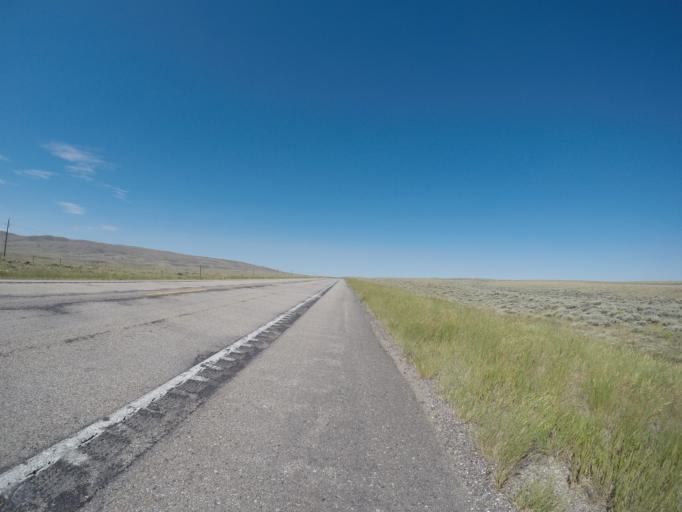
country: US
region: Wyoming
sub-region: Carbon County
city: Saratoga
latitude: 41.8040
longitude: -106.7004
